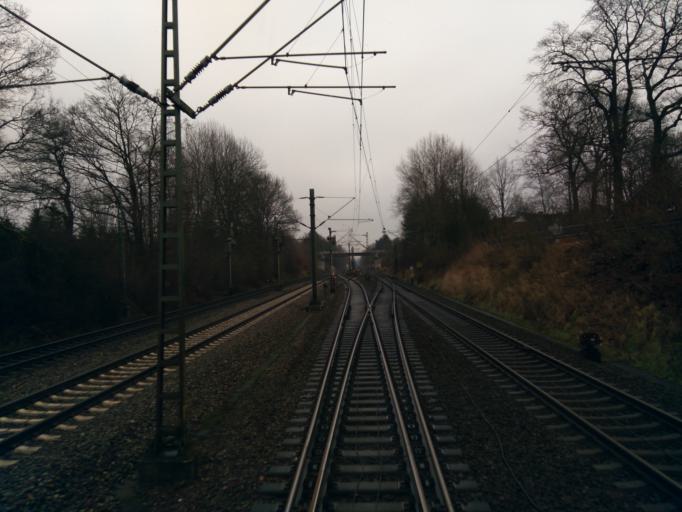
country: DE
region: Lower Saxony
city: Tostedt
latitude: 53.2765
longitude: 9.7419
